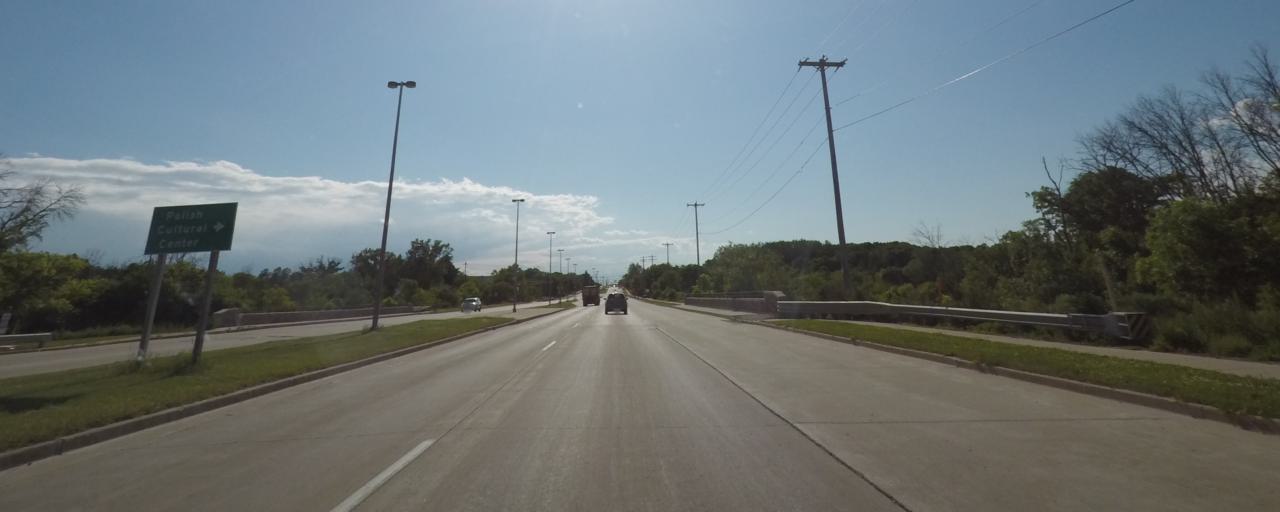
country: US
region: Wisconsin
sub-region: Milwaukee County
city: Greendale
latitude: 42.9160
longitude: -87.9962
